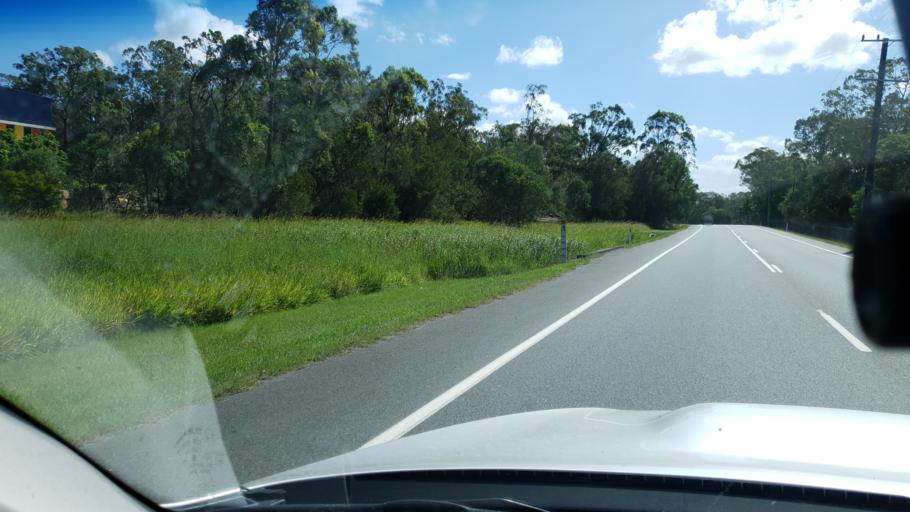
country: AU
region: Queensland
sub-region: Logan
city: Woodridge
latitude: -27.6472
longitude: 153.0892
